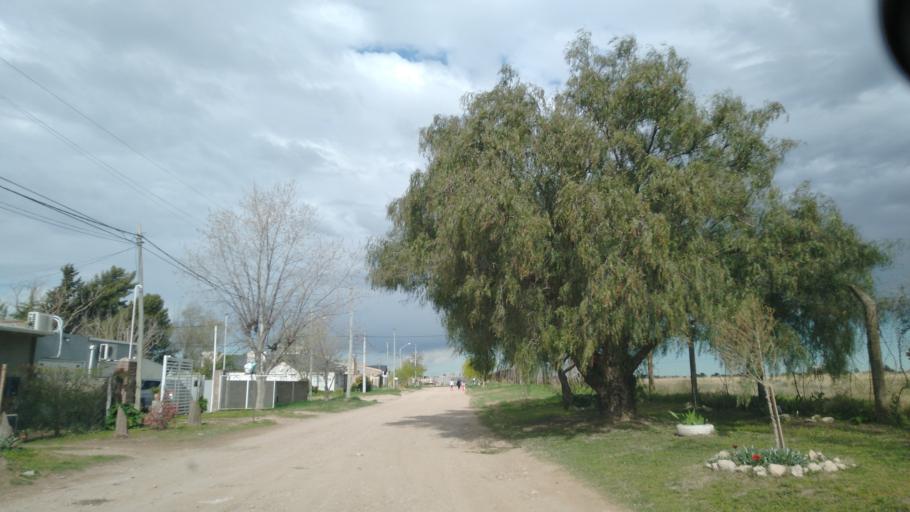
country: AR
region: Buenos Aires
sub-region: Partido de Bahia Blanca
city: Bahia Blanca
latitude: -38.7036
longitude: -62.2097
